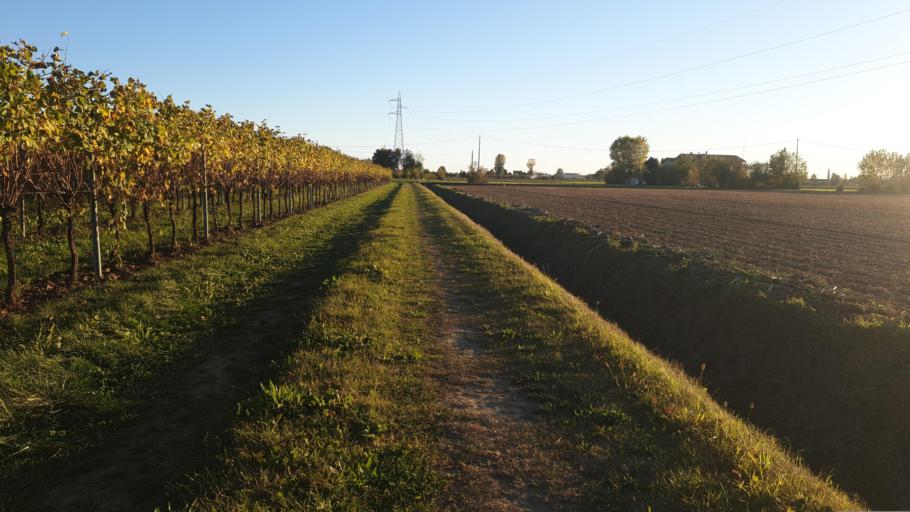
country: IT
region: Veneto
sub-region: Provincia di Venezia
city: Marano
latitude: 45.4497
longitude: 12.0990
